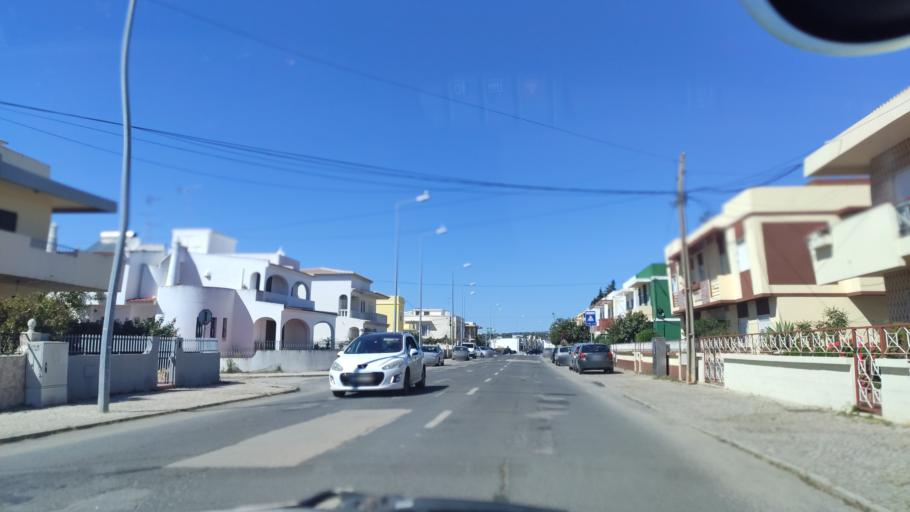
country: PT
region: Faro
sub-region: Olhao
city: Olhao
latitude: 37.0364
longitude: -7.8490
